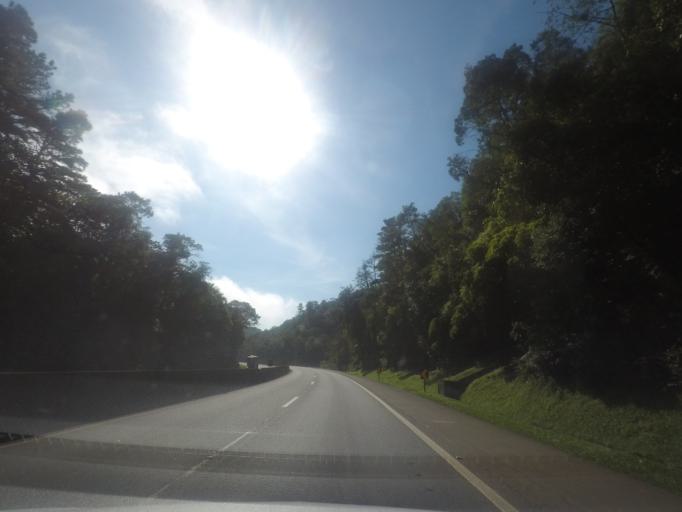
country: BR
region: Parana
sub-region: Piraquara
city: Piraquara
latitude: -25.5960
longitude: -48.8990
